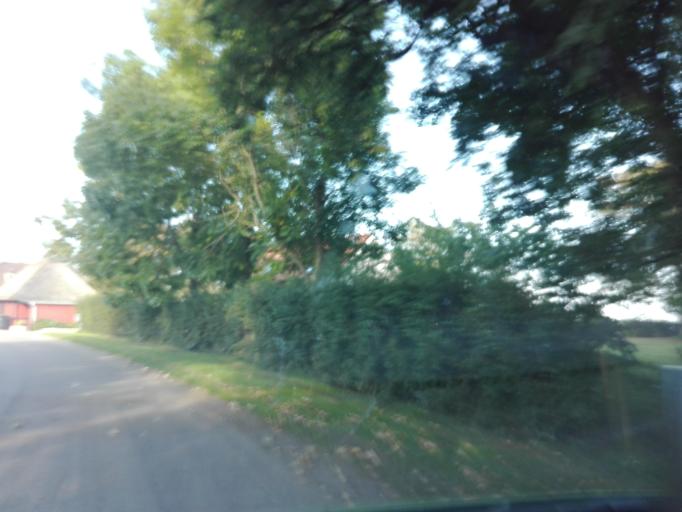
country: DK
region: Central Jutland
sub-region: Odder Kommune
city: Odder
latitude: 55.9054
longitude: 10.1885
